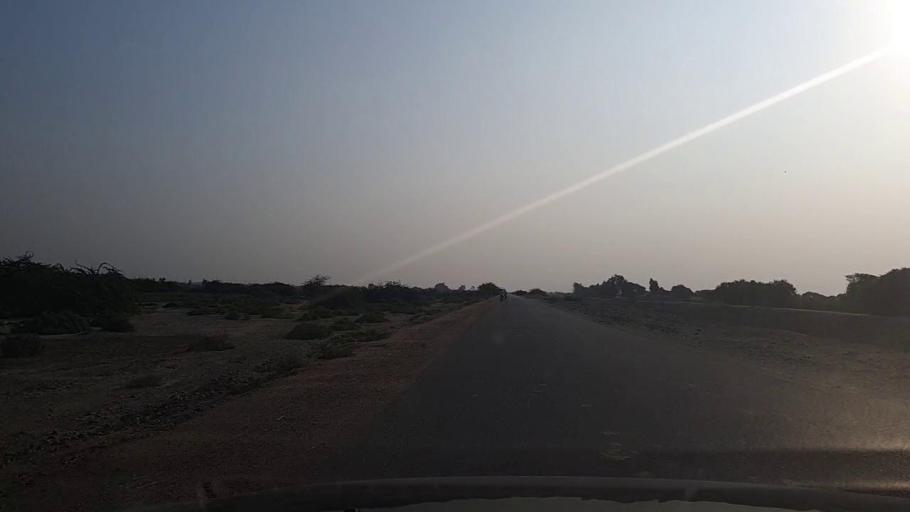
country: PK
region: Sindh
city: Mirpur Sakro
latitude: 24.4927
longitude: 67.8103
